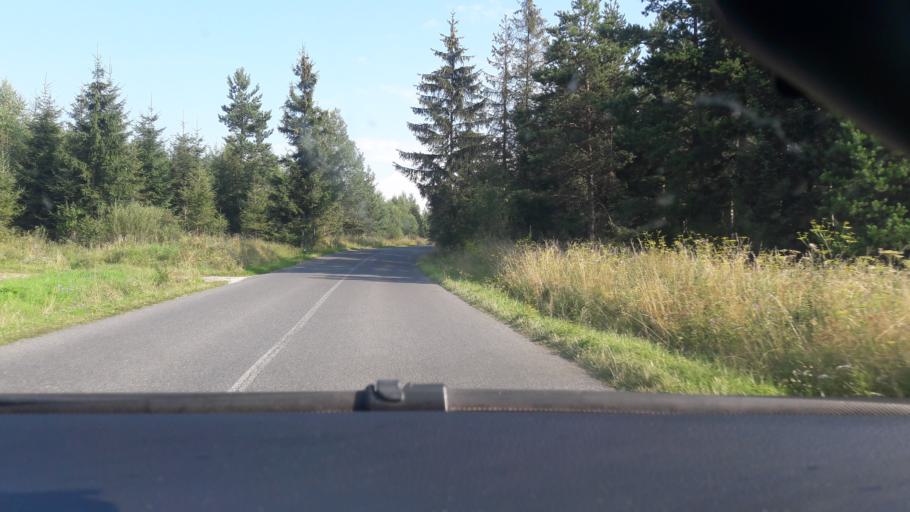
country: SK
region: Presovsky
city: Spisska Bela
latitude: 49.2048
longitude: 20.3733
